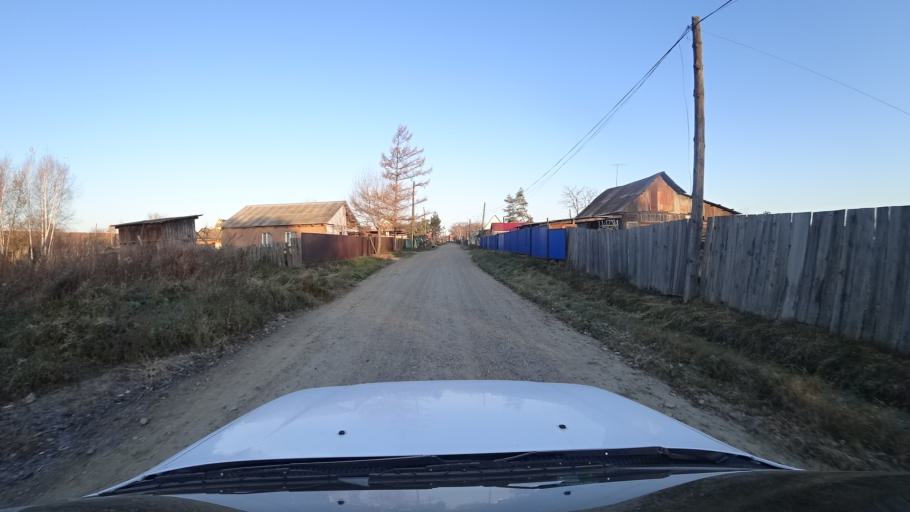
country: RU
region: Primorskiy
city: Dal'nerechensk
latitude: 45.9233
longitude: 133.7234
